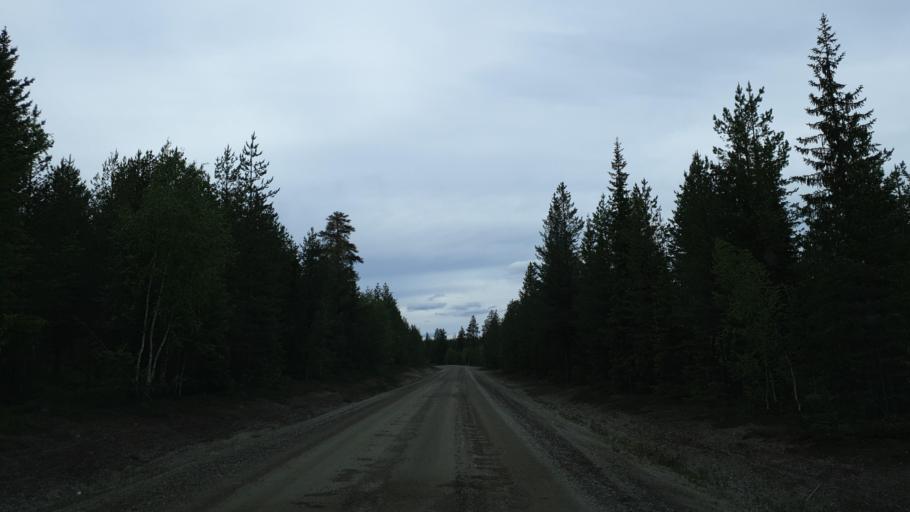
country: SE
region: Vaesterbotten
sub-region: Sorsele Kommun
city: Sorsele
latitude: 65.5537
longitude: 17.5067
